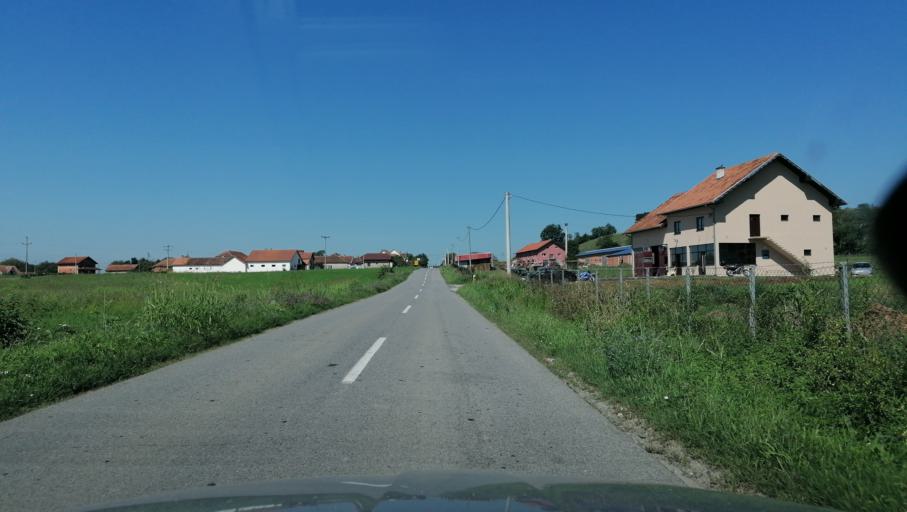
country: RS
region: Central Serbia
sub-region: Raski Okrug
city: Vrnjacka Banja
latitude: 43.6854
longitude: 20.8808
